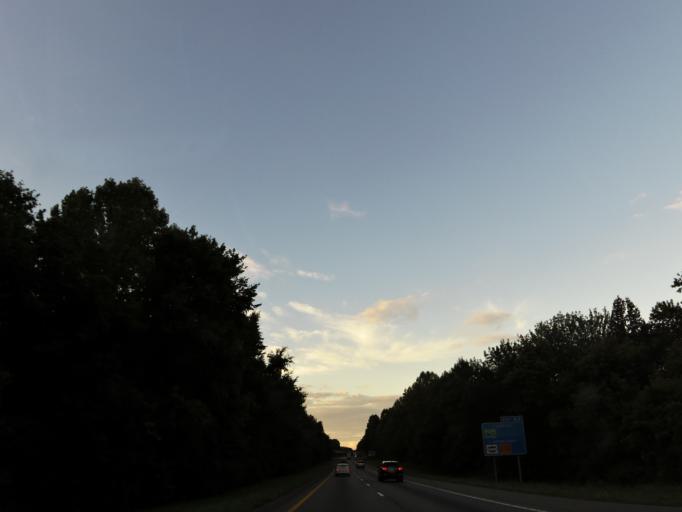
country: US
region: Tennessee
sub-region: McMinn County
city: Athens
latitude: 35.4446
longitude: -84.6704
